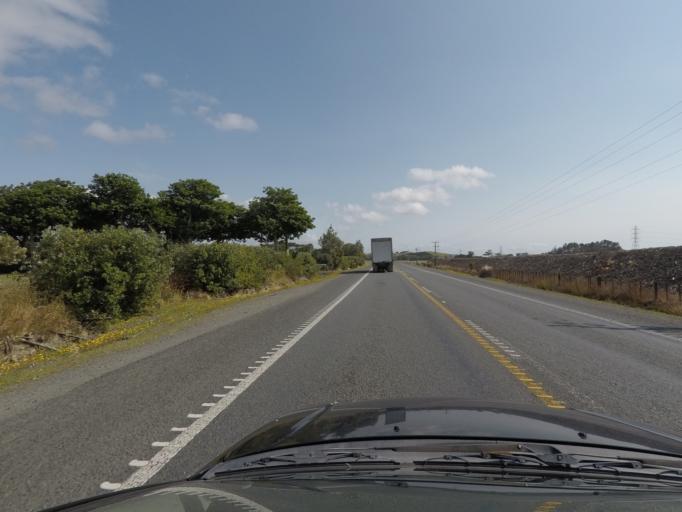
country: NZ
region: Northland
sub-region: Whangarei
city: Ruakaka
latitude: -36.0210
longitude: 174.4183
